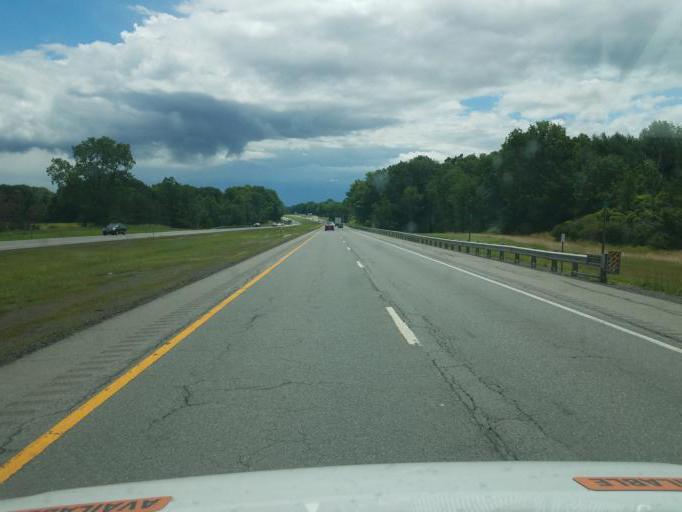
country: US
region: New York
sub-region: Monroe County
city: Pittsford
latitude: 43.0191
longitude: -77.4909
